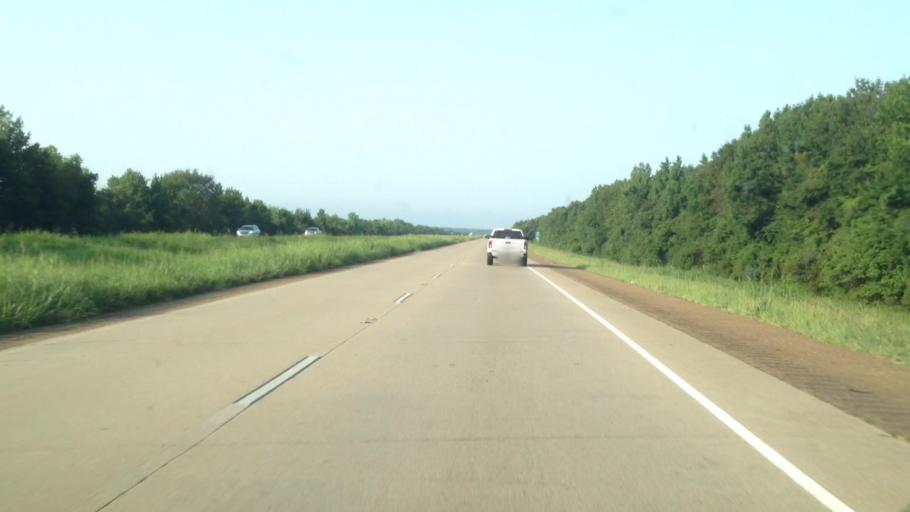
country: US
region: Louisiana
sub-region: Rapides Parish
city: Woodworth
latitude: 31.2265
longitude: -92.4658
